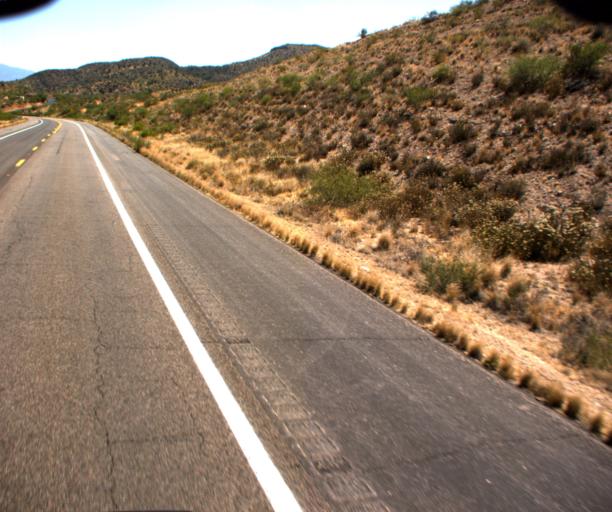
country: US
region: Arizona
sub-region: Gila County
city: Claypool
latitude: 33.4755
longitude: -110.8557
